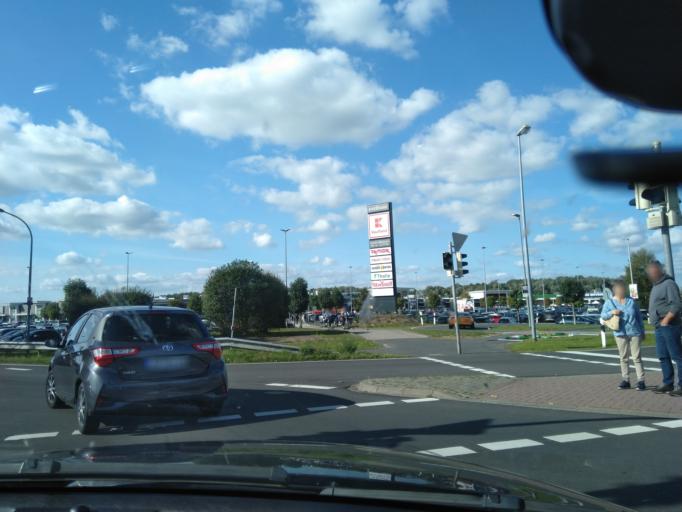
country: DE
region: Lower Saxony
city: Leer
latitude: 53.2590
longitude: 7.4594
